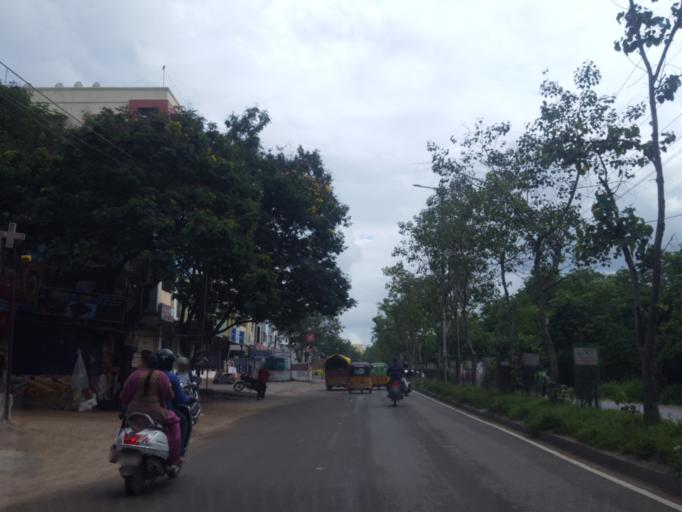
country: IN
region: Telangana
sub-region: Medak
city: Serilingampalle
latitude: 17.4898
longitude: 78.3140
